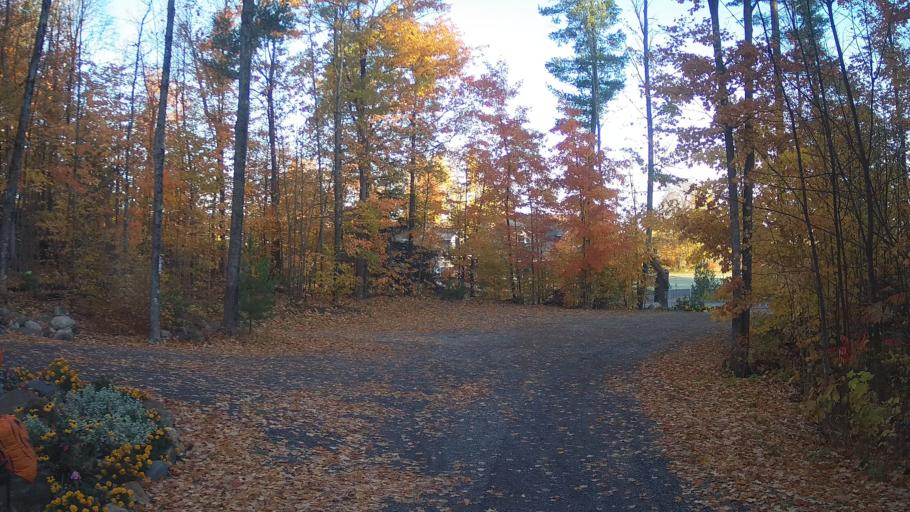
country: CA
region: Ontario
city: Arnprior
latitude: 45.3470
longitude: -76.3444
